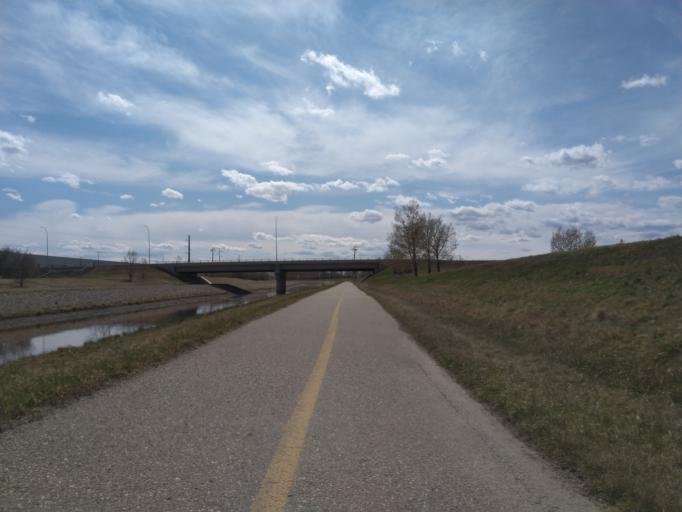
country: CA
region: Alberta
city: Chestermere
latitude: 50.9688
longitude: -113.9446
